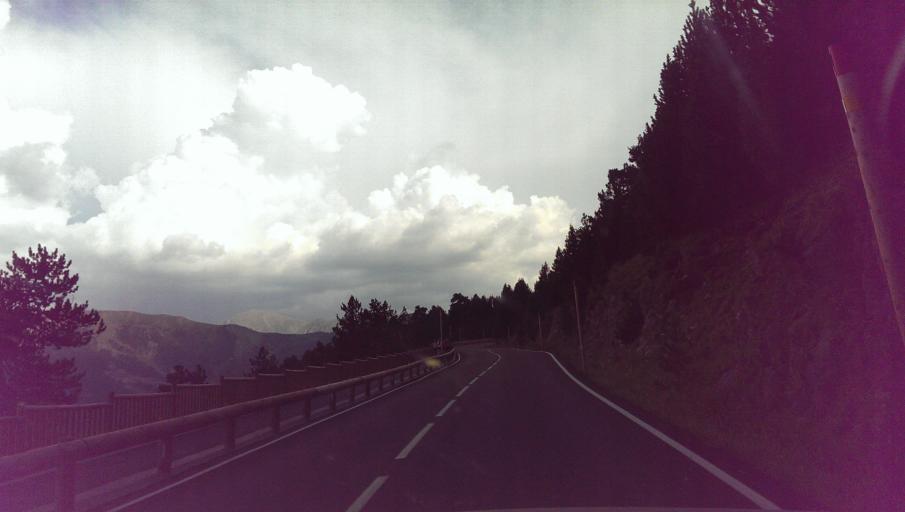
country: AD
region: Canillo
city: Canillo
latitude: 42.5705
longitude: 1.5871
